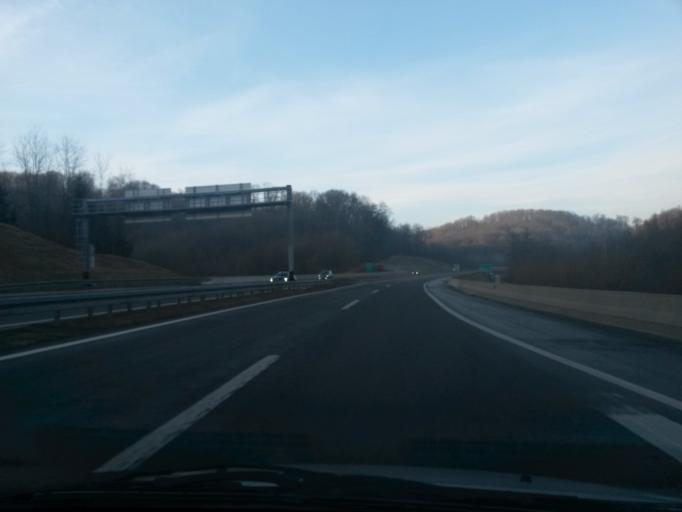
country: HR
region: Varazdinska
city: Ljubescica
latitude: 46.2114
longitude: 16.4056
